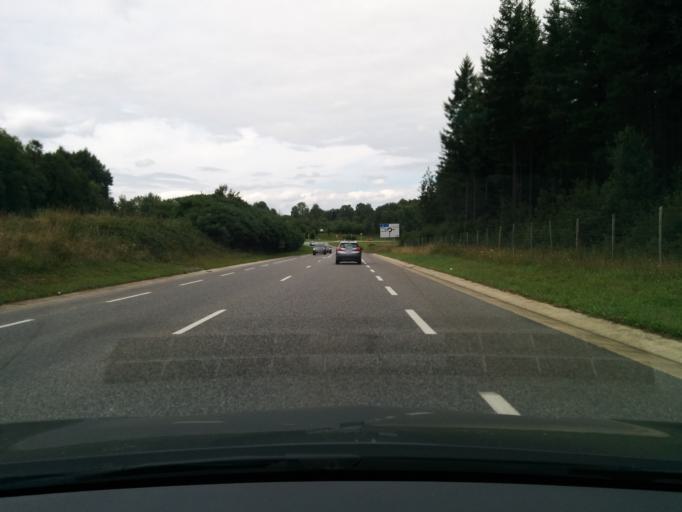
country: FR
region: Midi-Pyrenees
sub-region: Departement des Hautes-Pyrenees
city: La Barthe-de-Neste
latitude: 43.0780
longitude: 0.3624
